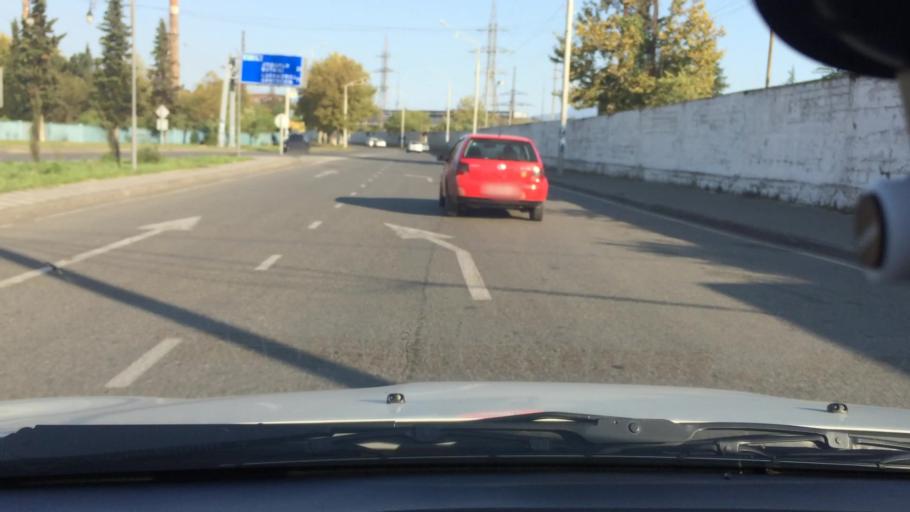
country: GE
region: Imereti
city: Zestap'oni
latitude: 42.1132
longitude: 43.0243
